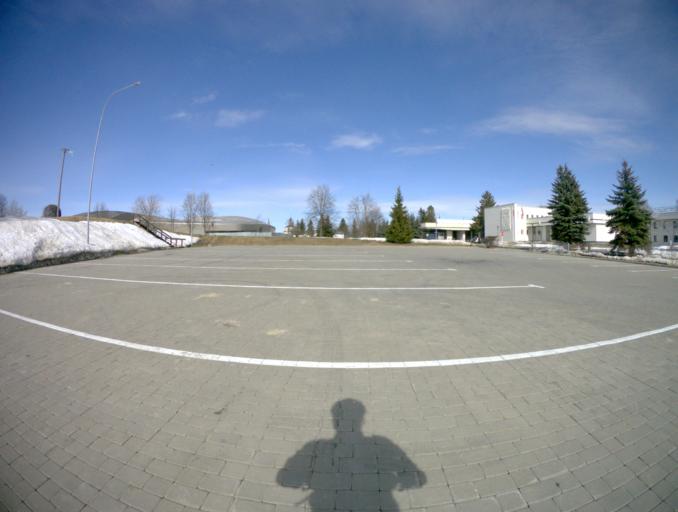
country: RU
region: Vladimir
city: Suzdal'
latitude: 56.4299
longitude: 40.4258
